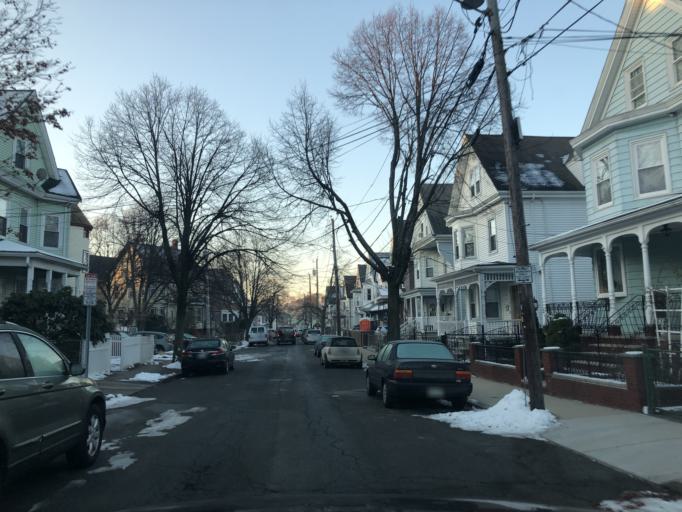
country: US
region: Massachusetts
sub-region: Middlesex County
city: Somerville
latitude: 42.3934
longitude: -71.1025
